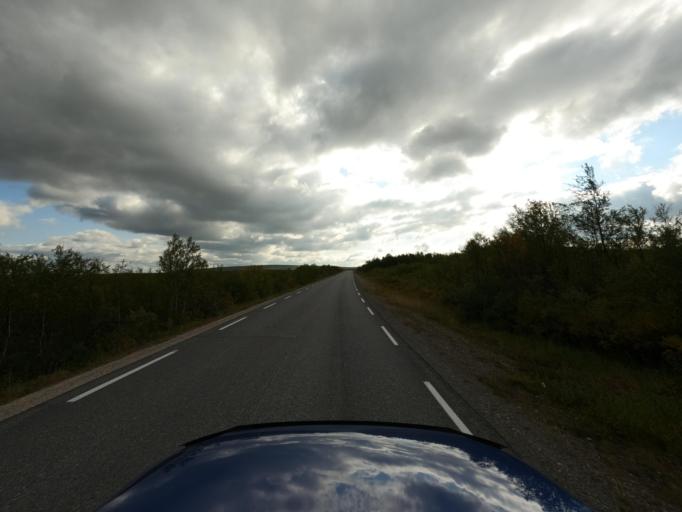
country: NO
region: Finnmark Fylke
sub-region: Porsanger
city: Lakselv
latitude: 69.3718
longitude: 24.2745
